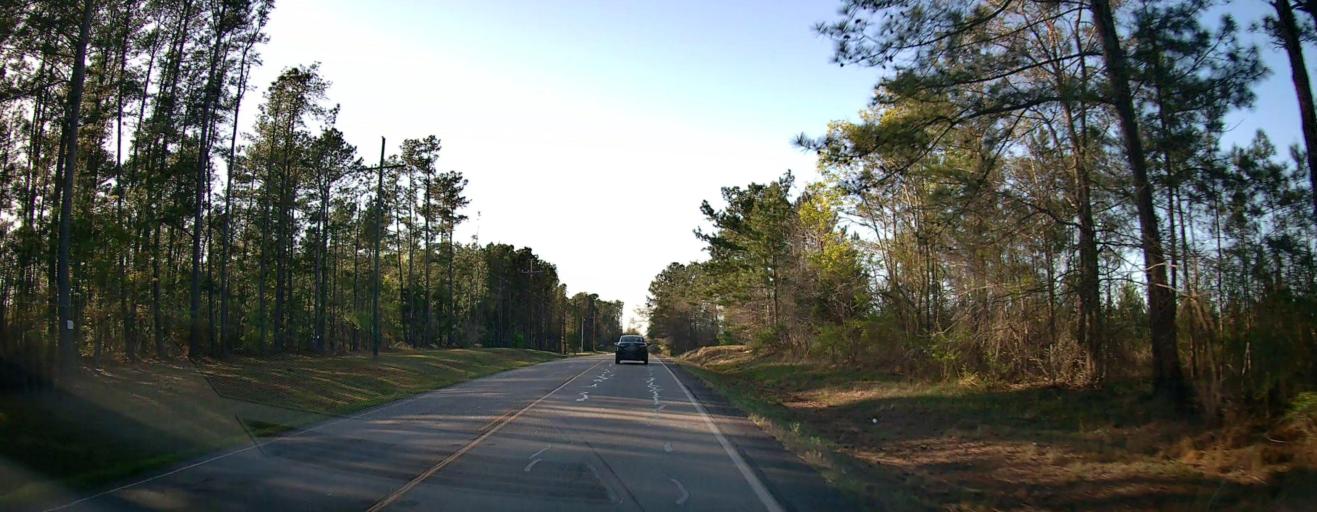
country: US
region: Georgia
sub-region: Butts County
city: Jackson
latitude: 33.4088
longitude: -83.8896
